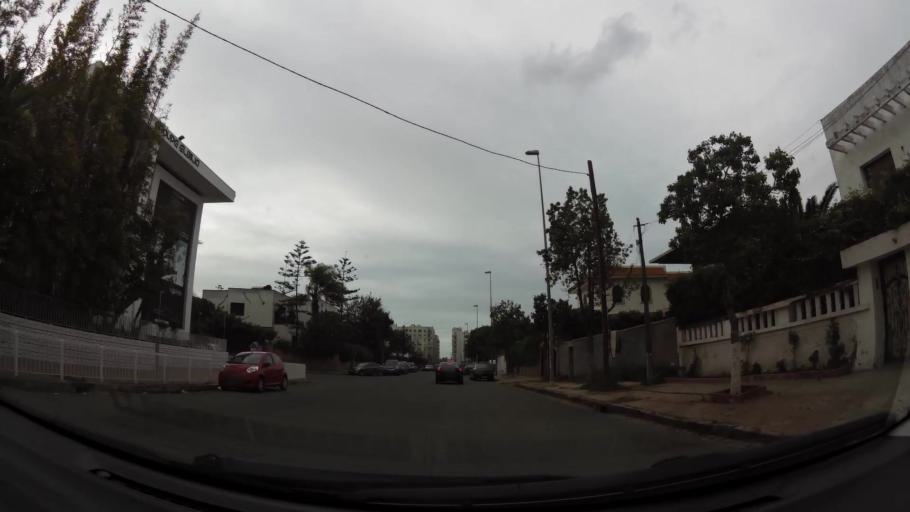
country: MA
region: Grand Casablanca
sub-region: Casablanca
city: Casablanca
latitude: 33.5933
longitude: -7.6489
